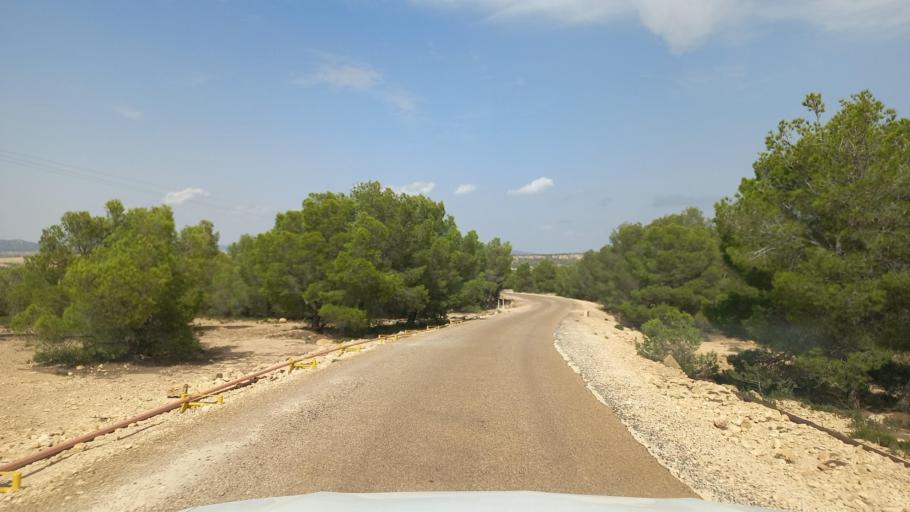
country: TN
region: Al Qasrayn
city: Sbiba
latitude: 35.3920
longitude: 8.9095
